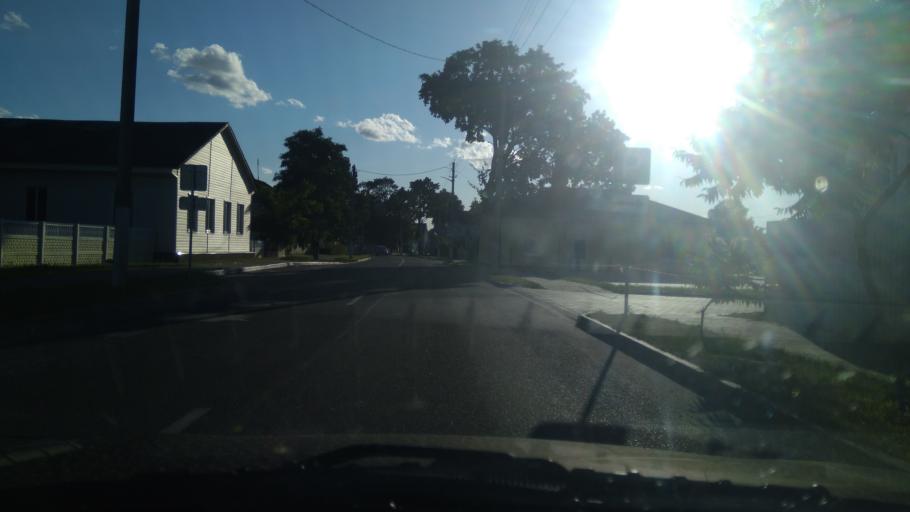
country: BY
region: Brest
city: Pruzhany
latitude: 52.5613
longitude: 24.4649
